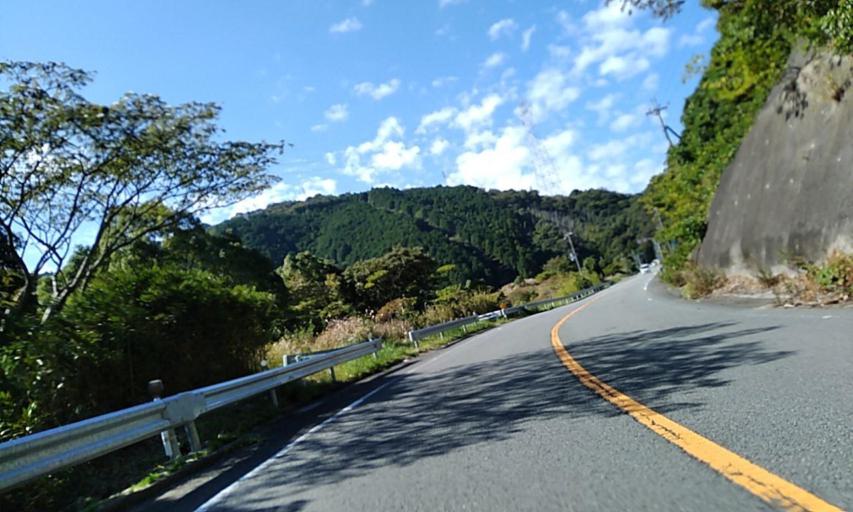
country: JP
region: Wakayama
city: Gobo
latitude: 33.9905
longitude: 135.1822
